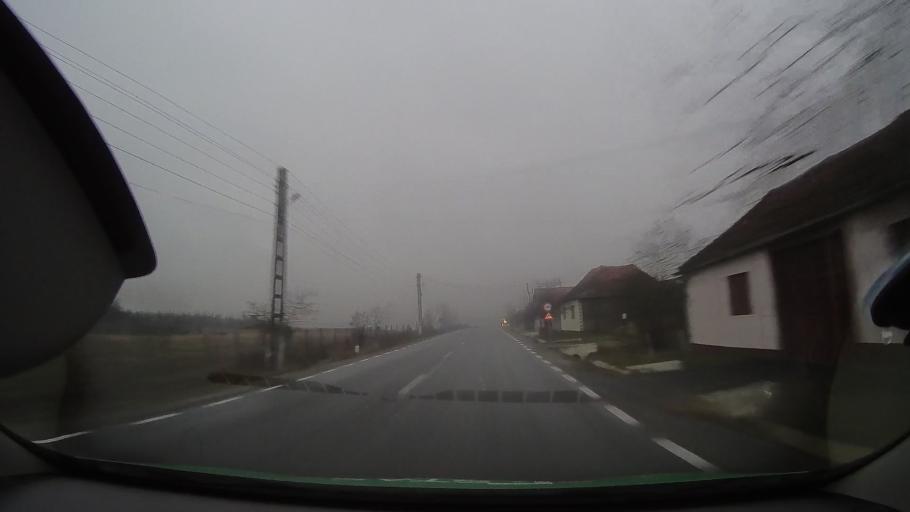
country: RO
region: Bihor
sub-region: Comuna Olcea
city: Olcea
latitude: 46.6838
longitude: 21.9663
